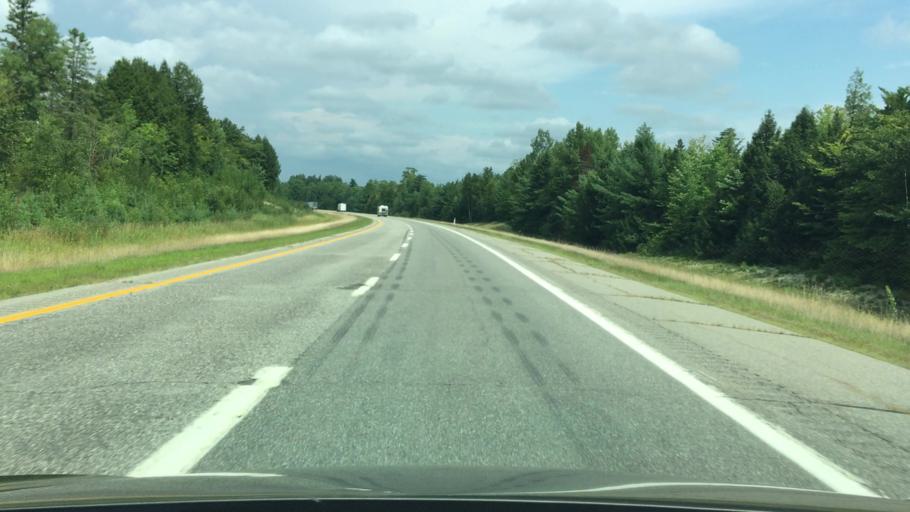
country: US
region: Maine
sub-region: Penobscot County
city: Lincoln
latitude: 45.3501
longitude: -68.6097
